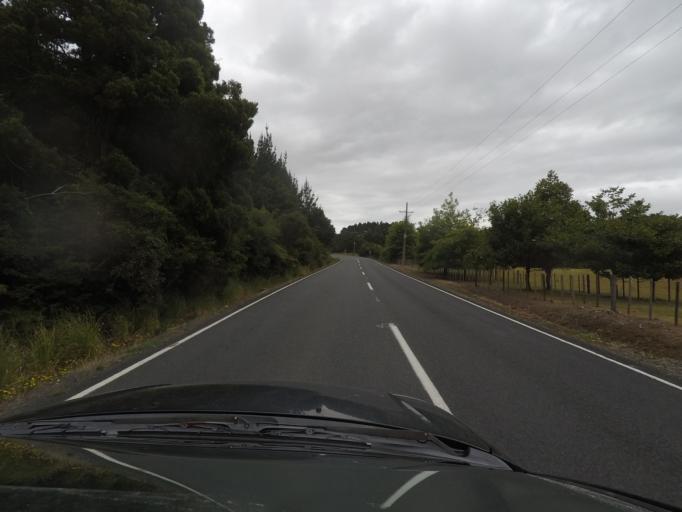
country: NZ
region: Auckland
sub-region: Auckland
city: Wellsford
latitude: -36.2919
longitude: 174.6145
